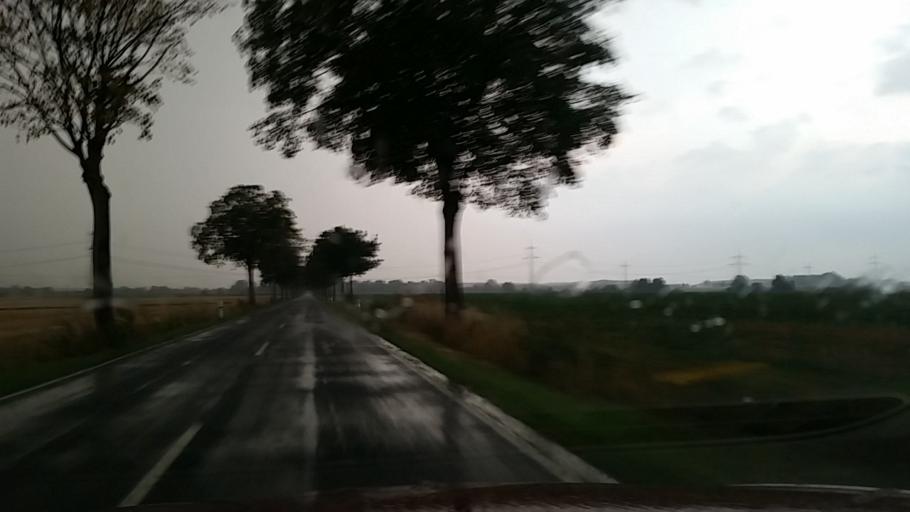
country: DE
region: Lower Saxony
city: Calberlah
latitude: 52.3818
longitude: 10.6440
